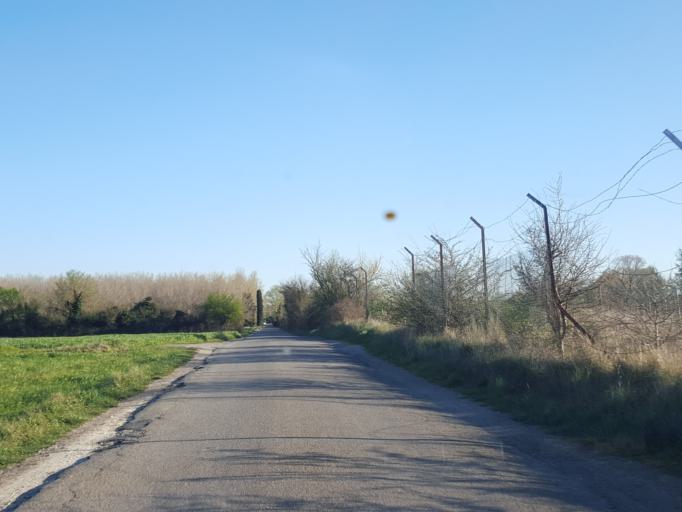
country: FR
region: Provence-Alpes-Cote d'Azur
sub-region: Departement du Vaucluse
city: Saint-Saturnin-les-Avignon
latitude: 43.9793
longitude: 4.9387
